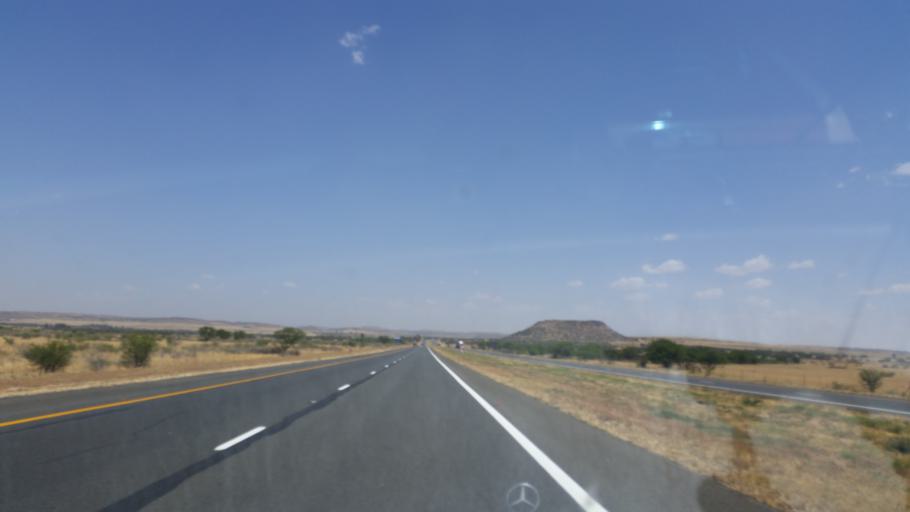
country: ZA
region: Orange Free State
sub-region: Lejweleputswa District Municipality
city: Brandfort
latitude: -28.9410
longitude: 26.4102
